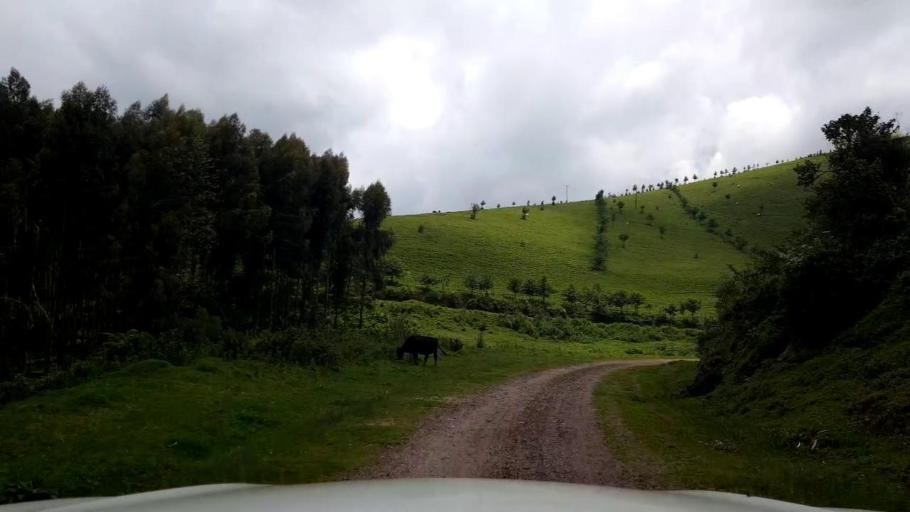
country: RW
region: Western Province
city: Gisenyi
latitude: -1.6874
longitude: 29.4224
